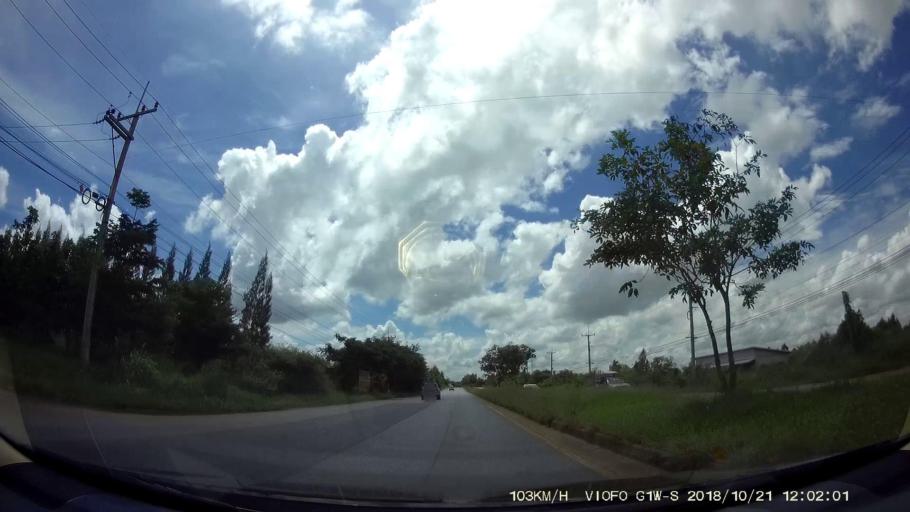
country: TH
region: Chaiyaphum
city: Chatturat
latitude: 15.5304
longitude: 101.8311
